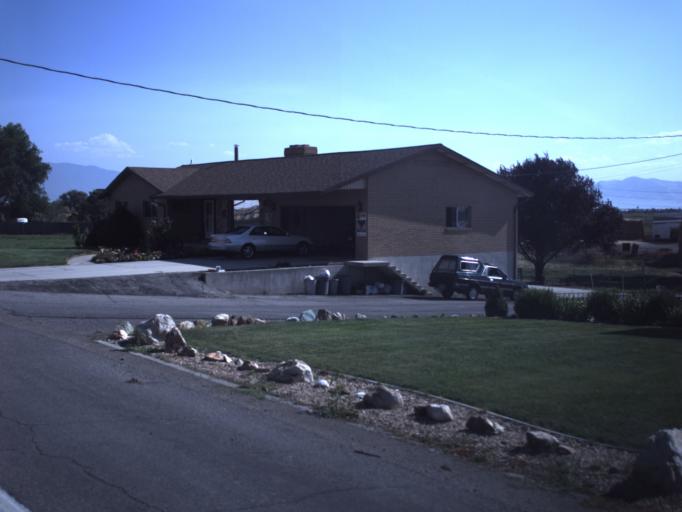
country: US
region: Utah
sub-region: Utah County
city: Orem
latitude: 40.2729
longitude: -111.7255
